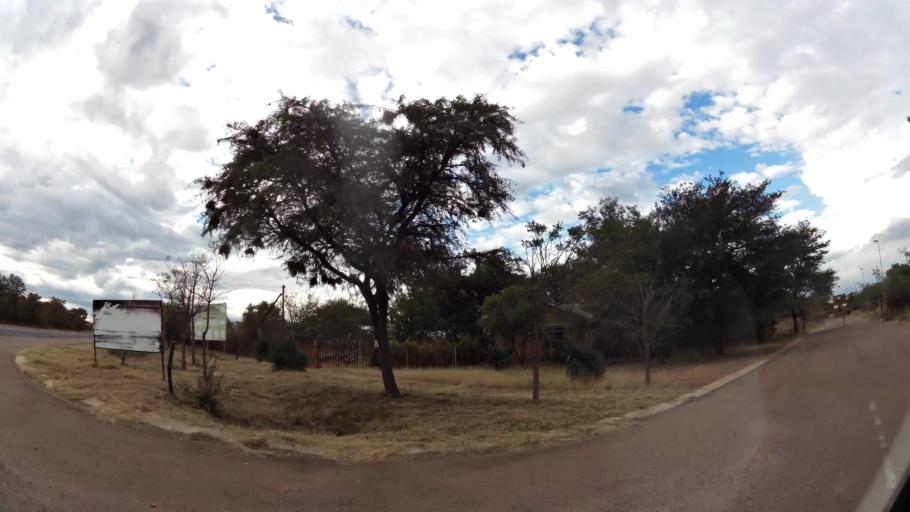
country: ZA
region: Limpopo
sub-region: Waterberg District Municipality
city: Modimolle
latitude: -24.5083
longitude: 28.7049
